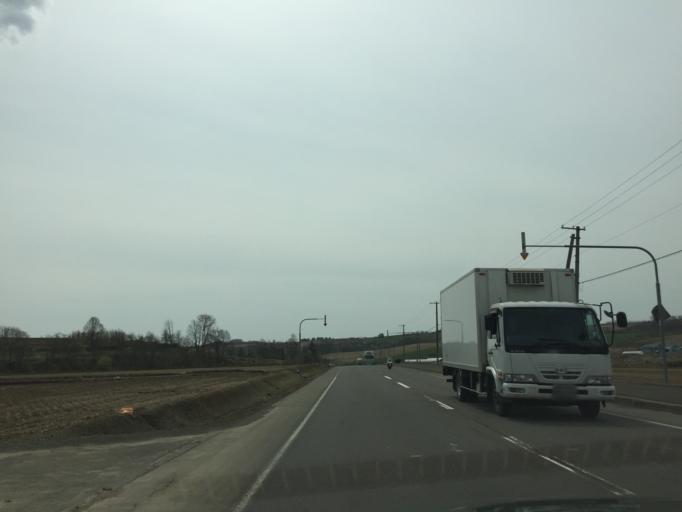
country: JP
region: Hokkaido
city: Ashibetsu
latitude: 43.6262
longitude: 142.1993
